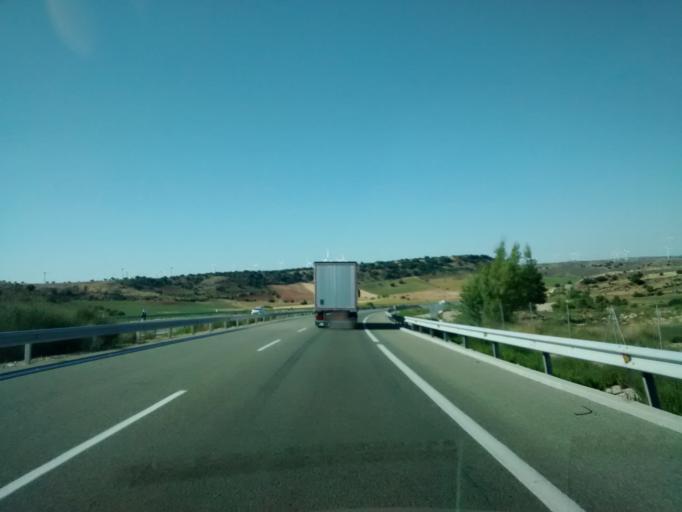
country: ES
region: Castille-La Mancha
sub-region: Provincia de Guadalajara
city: Alcolea del Pinar
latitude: 41.0535
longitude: -2.4484
